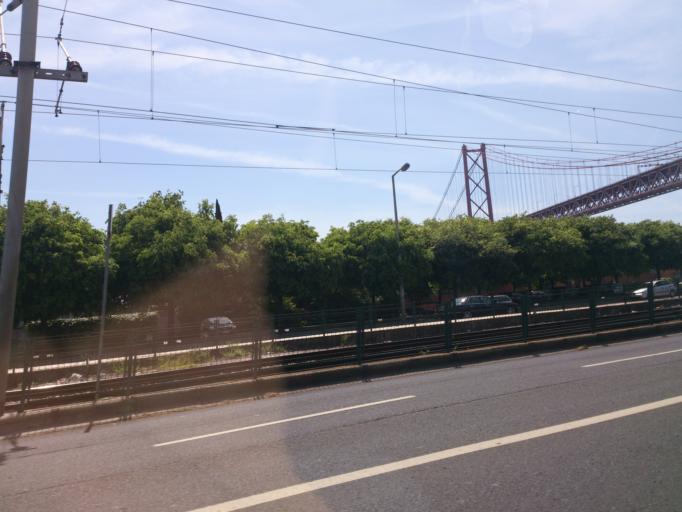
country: PT
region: Setubal
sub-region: Almada
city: Pragal
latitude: 38.7013
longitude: -9.1766
